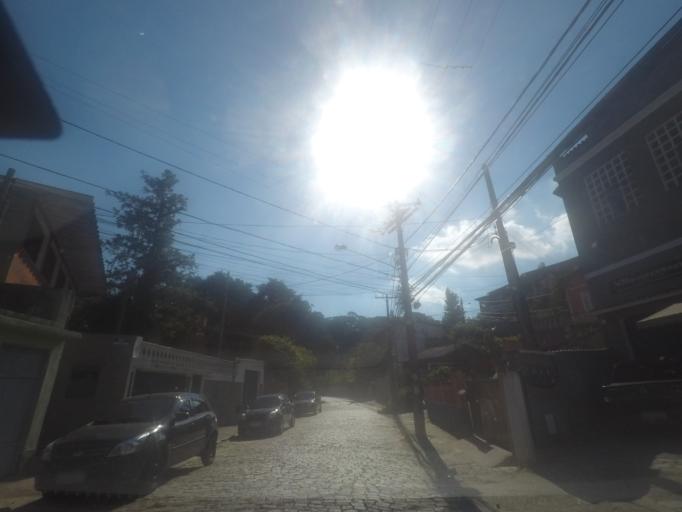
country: BR
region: Rio de Janeiro
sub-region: Petropolis
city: Petropolis
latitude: -22.5363
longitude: -43.1984
